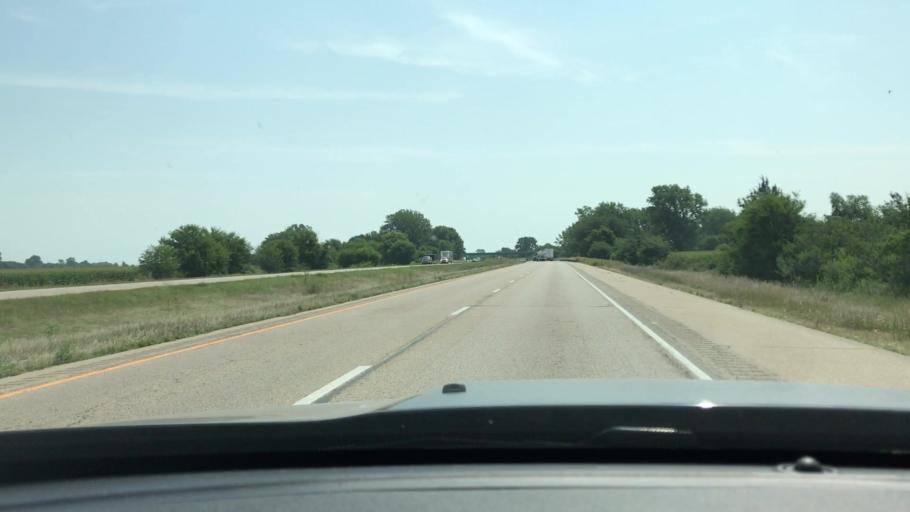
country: US
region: Illinois
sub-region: Henry County
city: Kewanee
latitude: 41.3900
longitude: -89.8416
